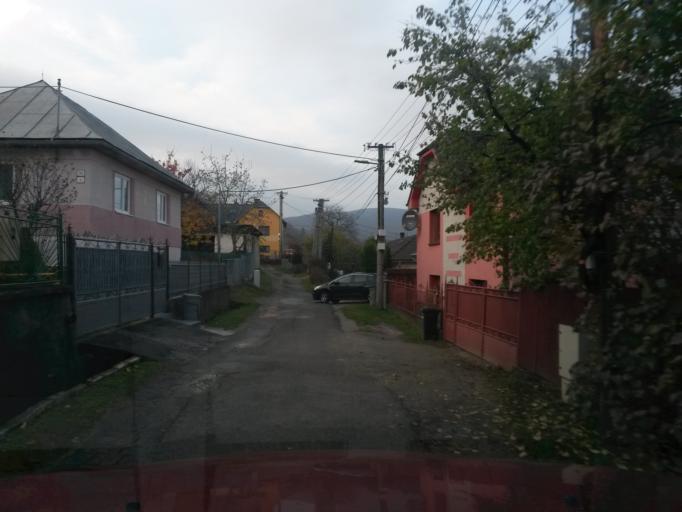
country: SK
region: Kosicky
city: Kosice
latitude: 48.7772
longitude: 21.2028
